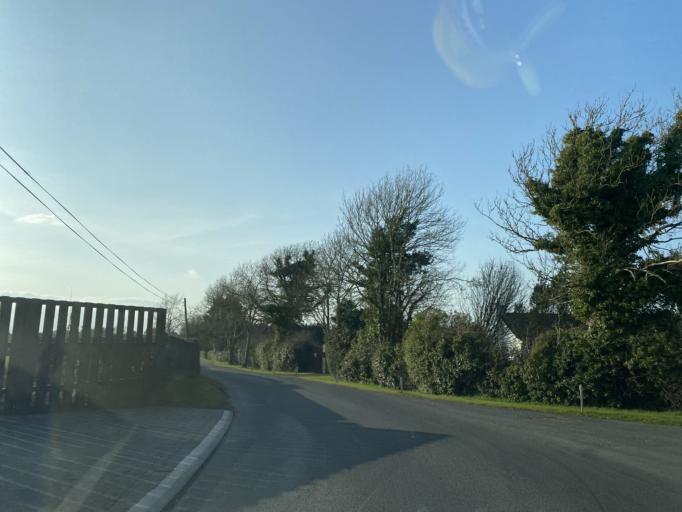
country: IE
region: Leinster
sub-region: Kildare
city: Maynooth
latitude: 53.3640
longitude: -6.5727
